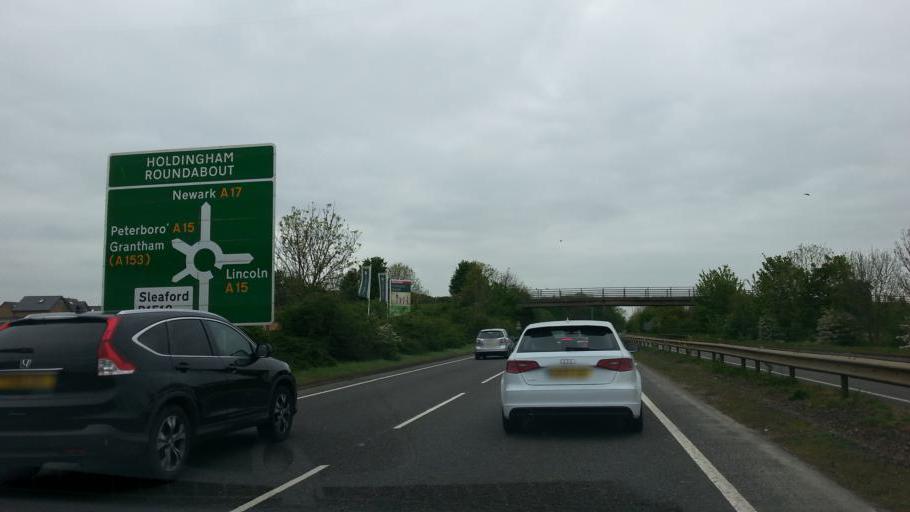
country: GB
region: England
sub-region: Lincolnshire
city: Leasingham
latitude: 53.0132
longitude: -0.4191
